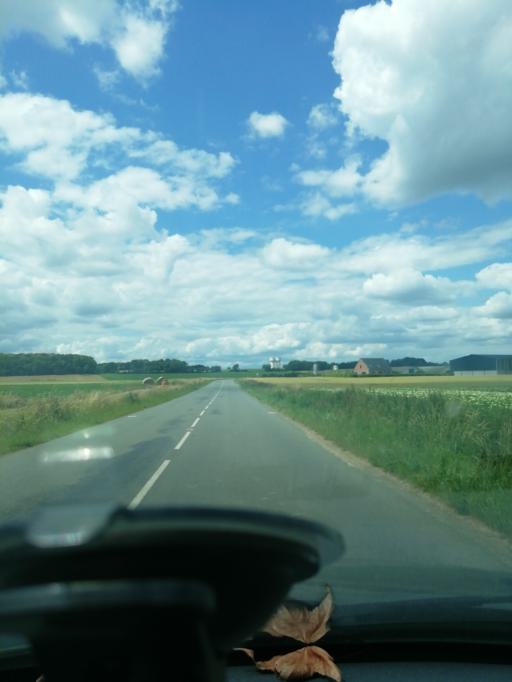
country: FR
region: Nord-Pas-de-Calais
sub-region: Departement du Nord
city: Lewarde
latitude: 50.3085
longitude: 3.1741
